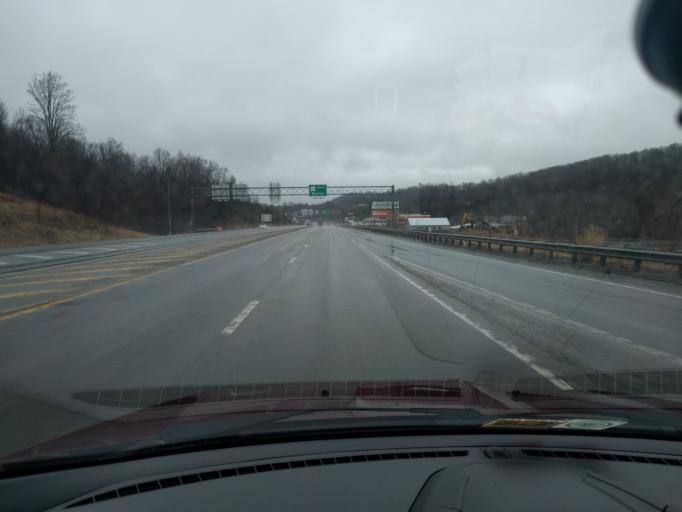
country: US
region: West Virginia
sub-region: Raleigh County
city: Sophia
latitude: 37.7246
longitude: -81.2484
